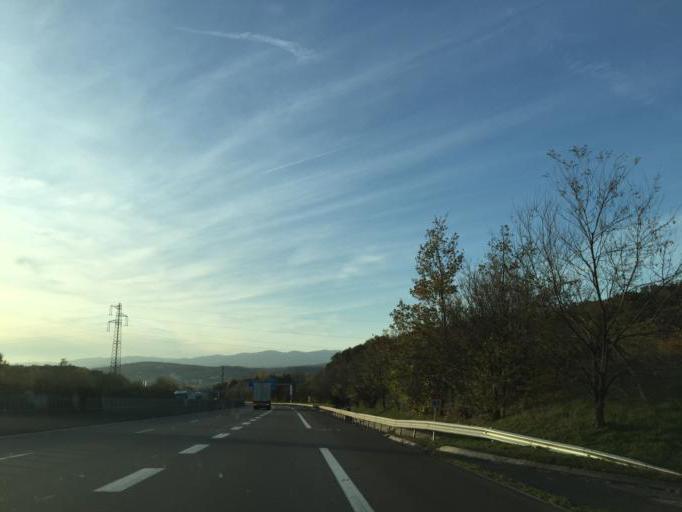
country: FR
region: Rhone-Alpes
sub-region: Departement de l'Isere
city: Chasse-sur-Rhone
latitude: 45.5890
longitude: 4.8115
